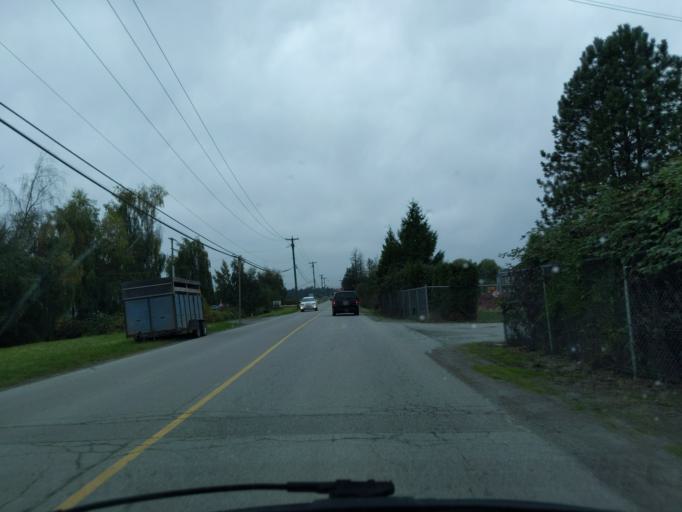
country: CA
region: British Columbia
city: Pitt Meadows
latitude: 49.2226
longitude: -122.7139
